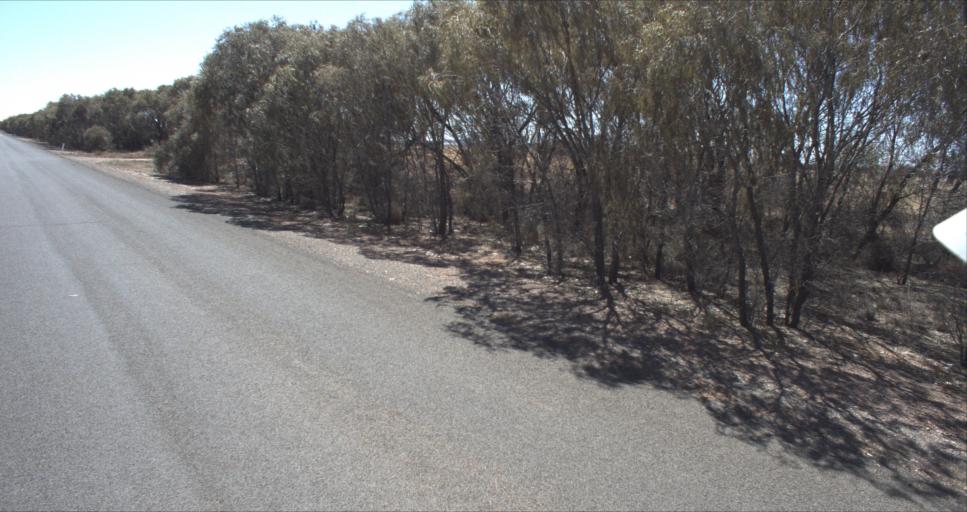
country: AU
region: New South Wales
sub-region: Leeton
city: Leeton
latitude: -34.4861
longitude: 146.2896
